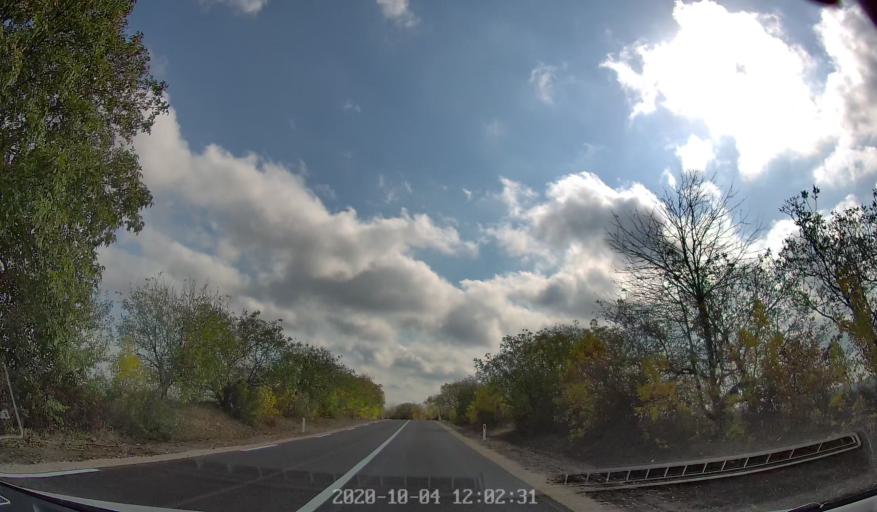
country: MD
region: Rezina
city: Saharna
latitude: 47.6163
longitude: 28.9088
